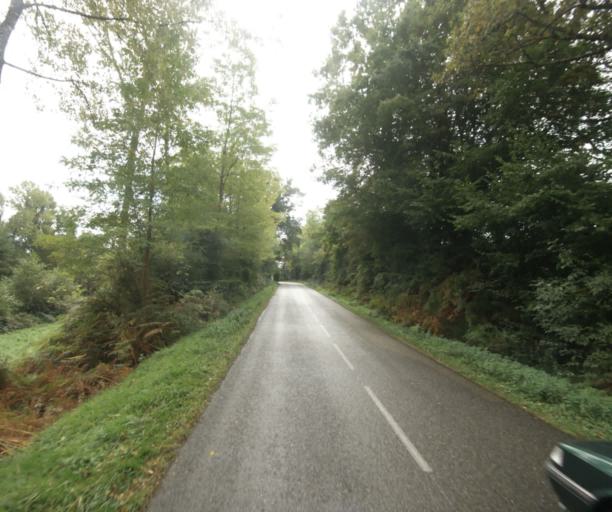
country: FR
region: Midi-Pyrenees
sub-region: Departement du Gers
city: Cazaubon
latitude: 43.8913
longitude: -0.0957
